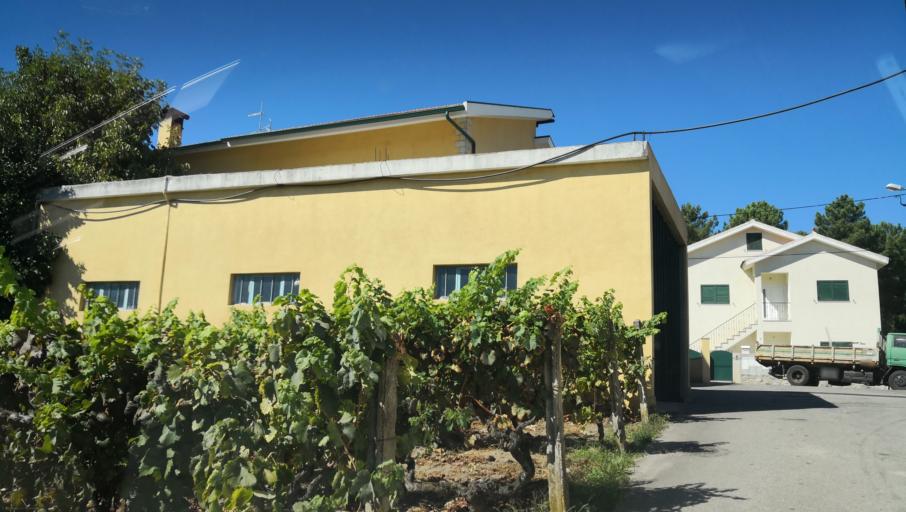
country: PT
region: Vila Real
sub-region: Vila Real
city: Vila Real
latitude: 41.3183
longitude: -7.7252
